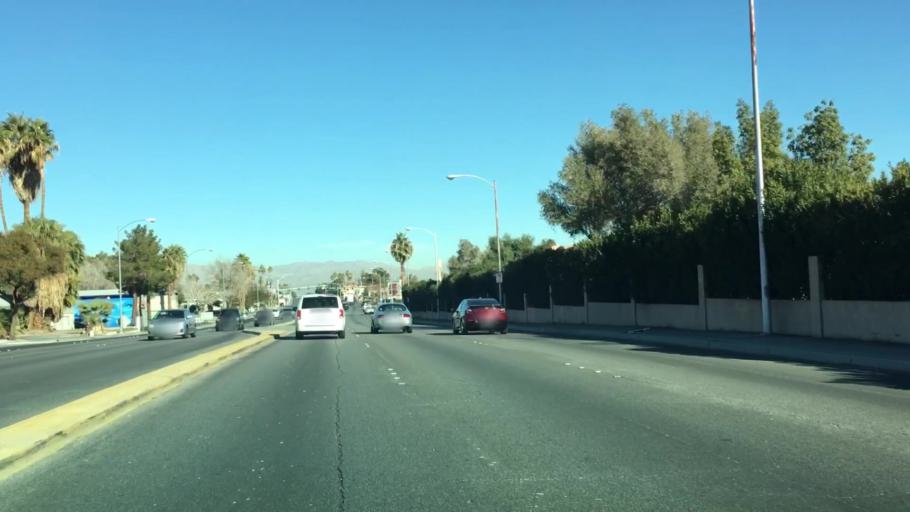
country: US
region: Nevada
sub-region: Clark County
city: Winchester
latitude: 36.1267
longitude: -115.1186
